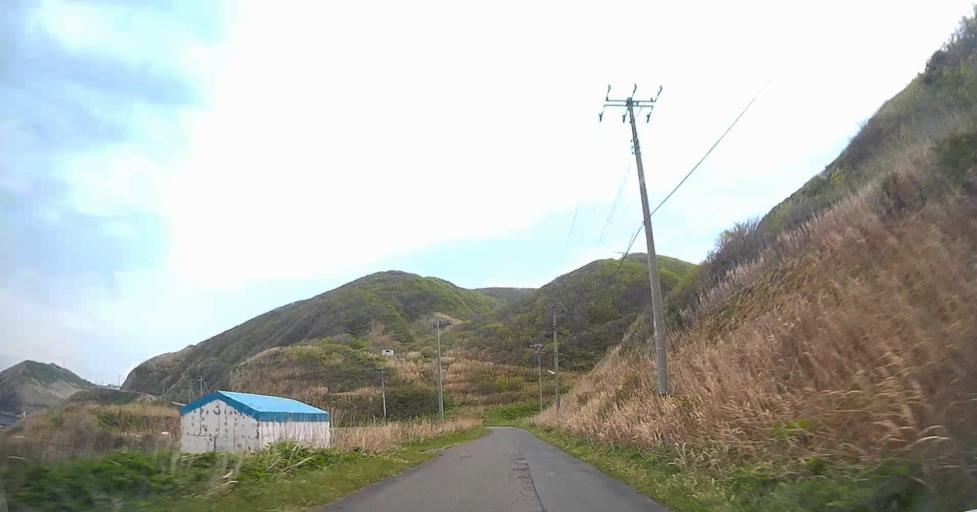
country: JP
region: Aomori
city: Shimokizukuri
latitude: 41.2452
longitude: 140.3431
